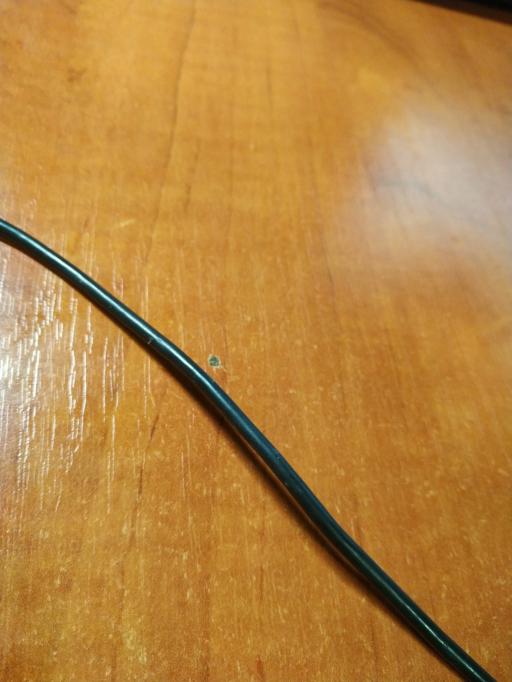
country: RU
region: Novgorod
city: Uglovka
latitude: 58.3274
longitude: 33.5519
